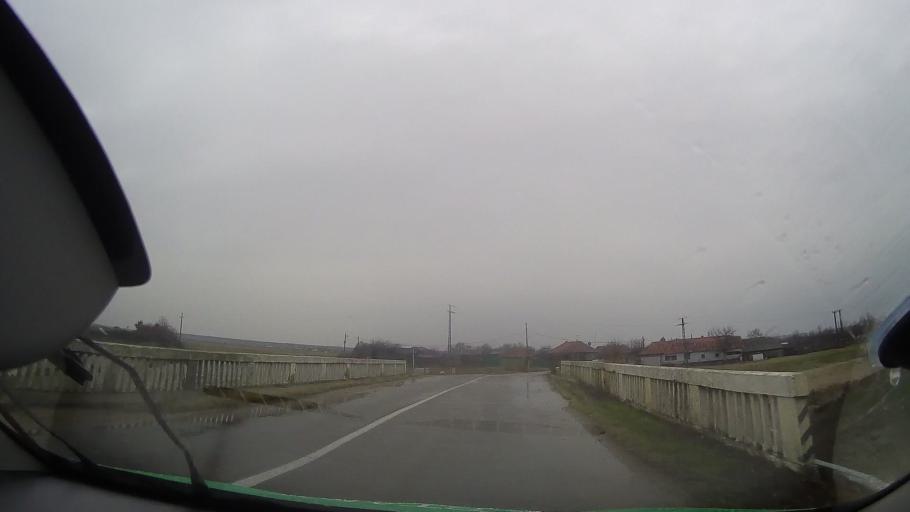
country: RO
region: Bihor
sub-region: Comuna Tinca
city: Gurbediu
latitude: 46.7825
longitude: 21.8681
